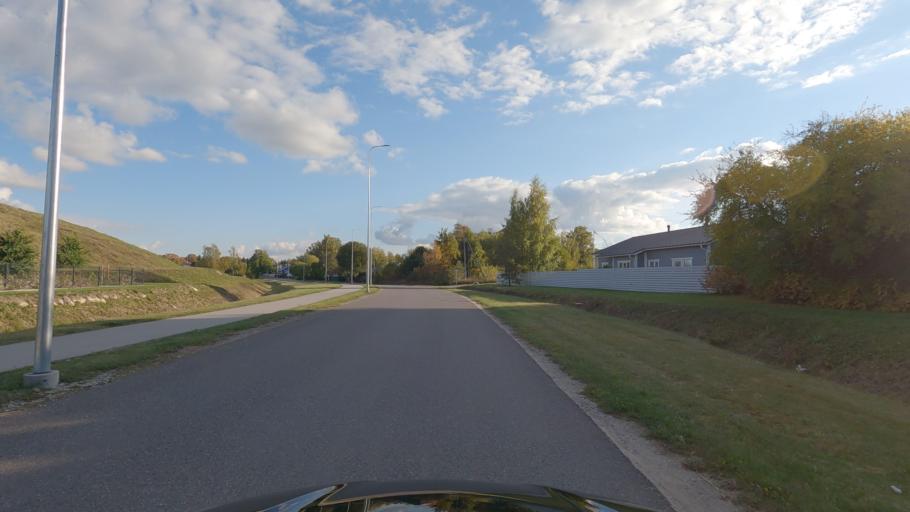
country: EE
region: Harju
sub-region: Saku vald
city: Saku
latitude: 59.3040
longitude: 24.6500
